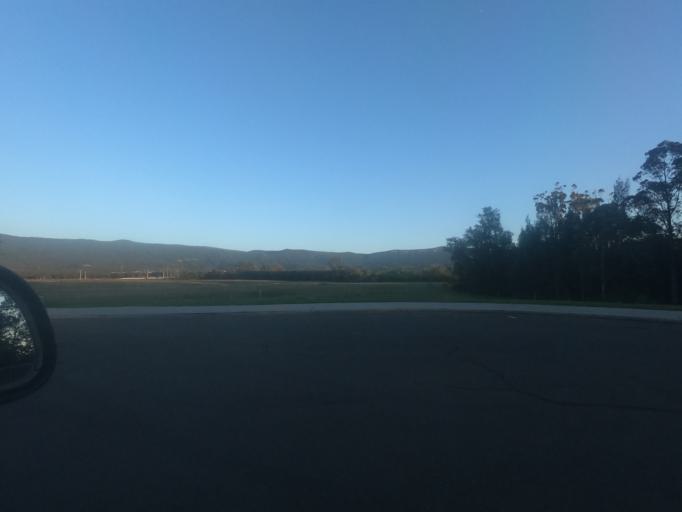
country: AU
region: New South Wales
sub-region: Wollongong
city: Dapto
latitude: -34.5013
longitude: 150.7846
